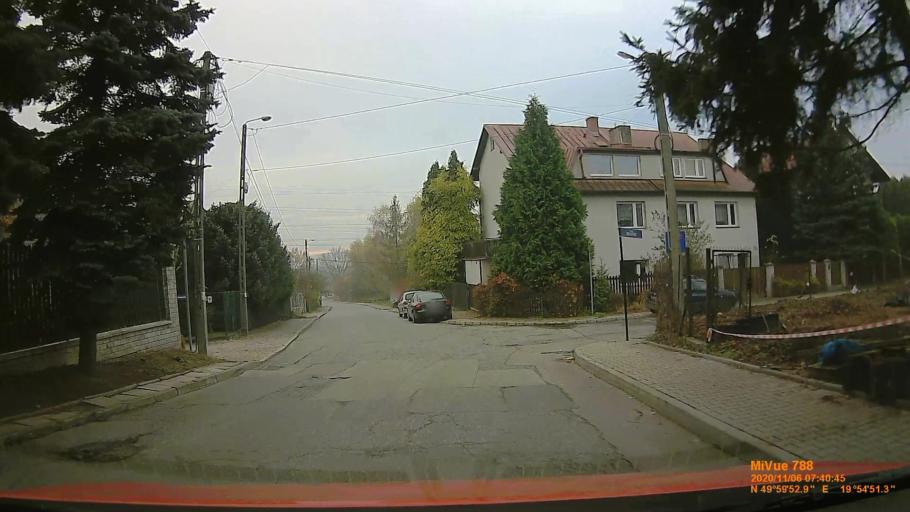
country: PL
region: Lesser Poland Voivodeship
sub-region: Powiat krakowski
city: Libertow
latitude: 49.9980
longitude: 19.9143
